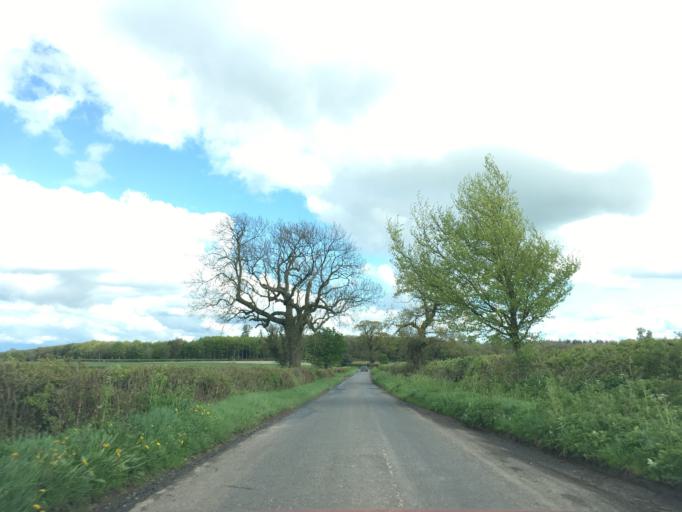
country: GB
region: England
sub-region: Wiltshire
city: Luckington
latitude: 51.5848
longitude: -2.2830
